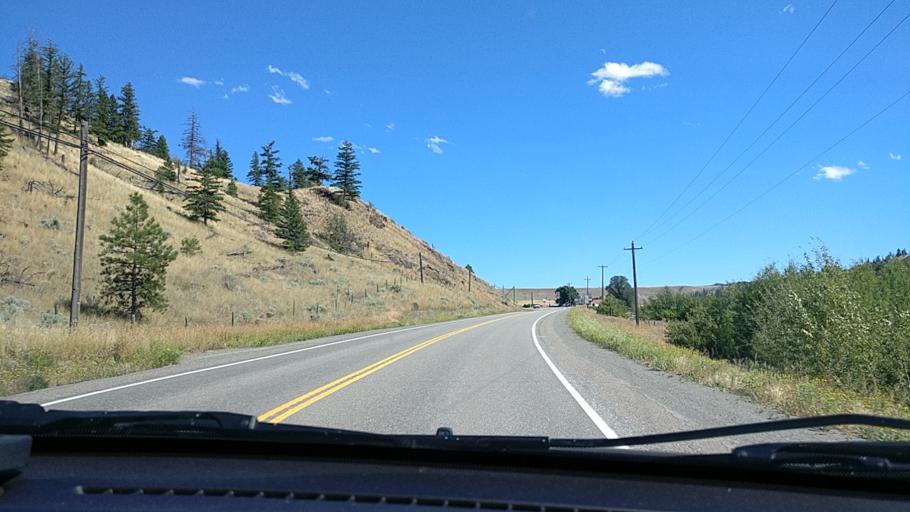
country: CA
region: British Columbia
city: Kamloops
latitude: 50.6651
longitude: -120.5589
